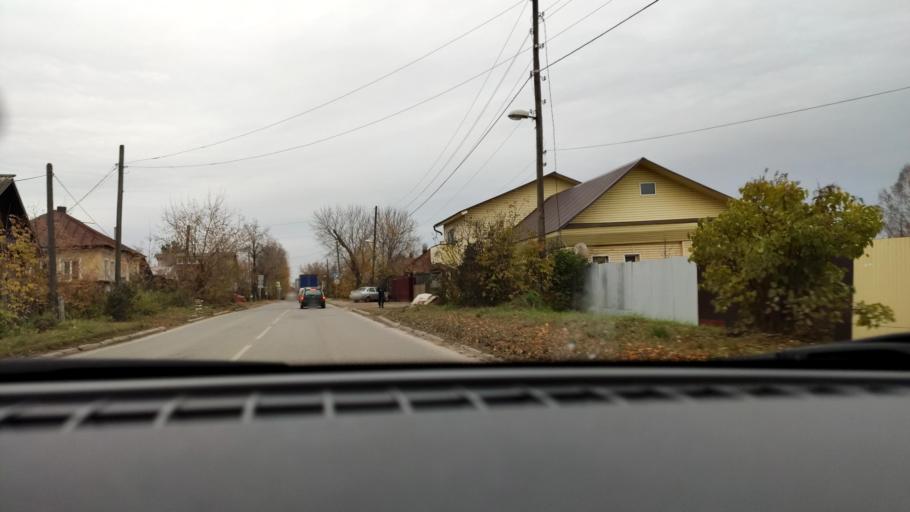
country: RU
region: Perm
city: Perm
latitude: 58.0155
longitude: 56.3167
